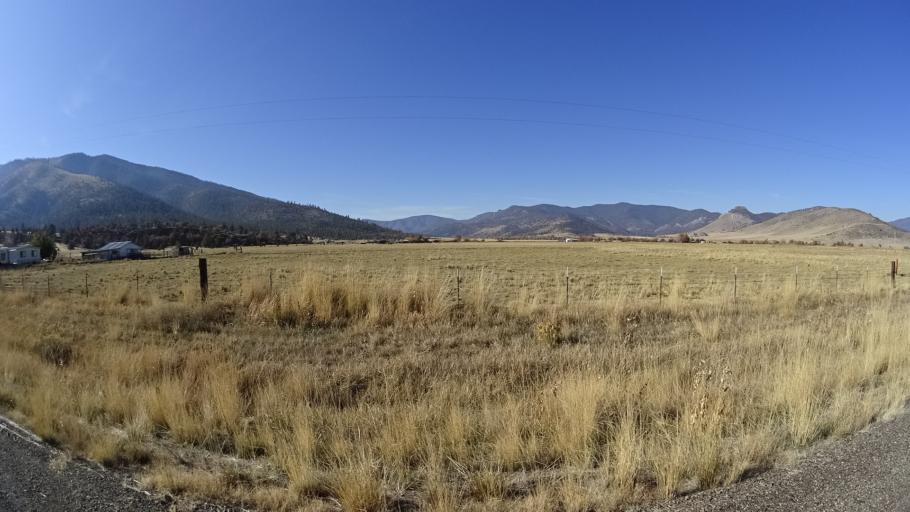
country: US
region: California
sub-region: Siskiyou County
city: Weed
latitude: 41.4991
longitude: -122.5134
